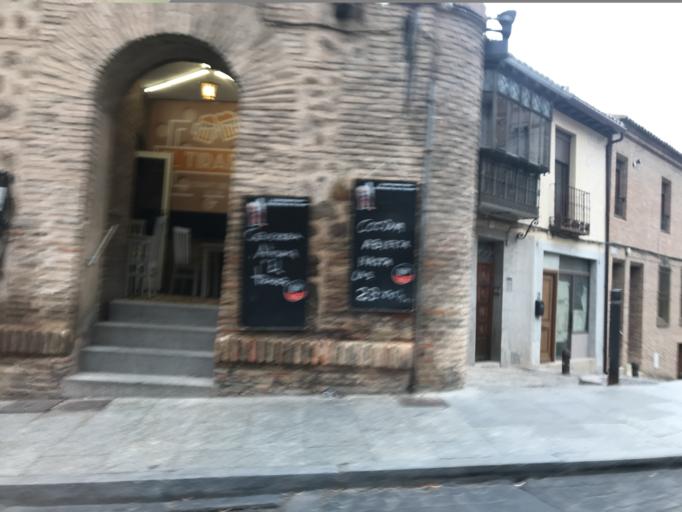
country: ES
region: Castille-La Mancha
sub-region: Province of Toledo
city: Toledo
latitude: 39.8613
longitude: -4.0248
